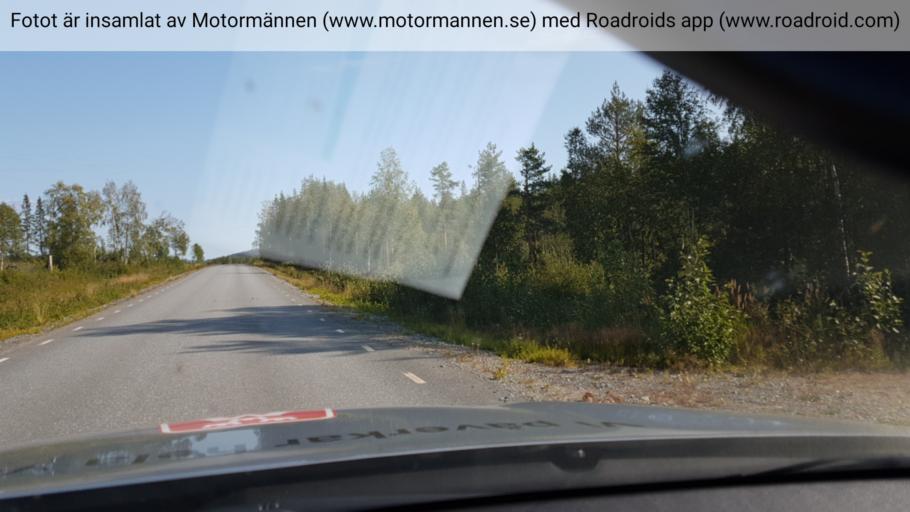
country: SE
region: Norrbotten
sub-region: Alvsbyns Kommun
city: AElvsbyn
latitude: 65.6082
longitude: 20.8832
